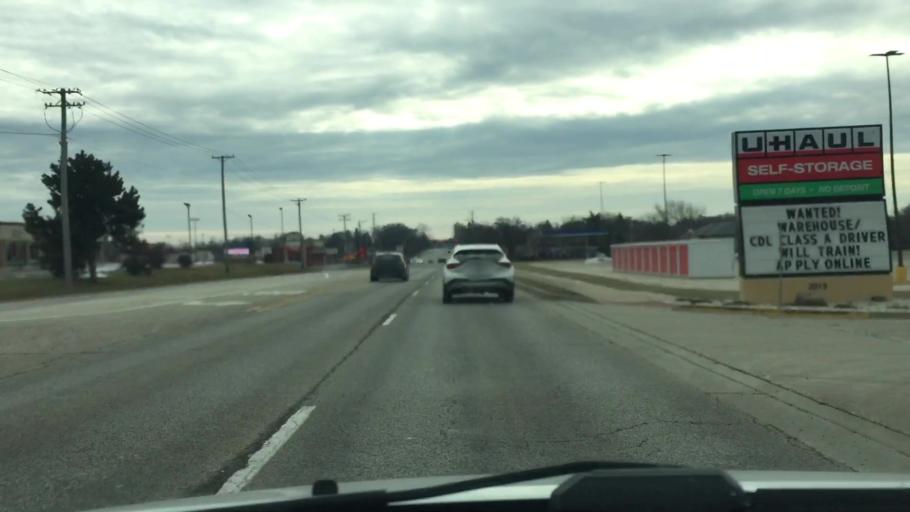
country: US
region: Illinois
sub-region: McHenry County
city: McHenry
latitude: 42.3567
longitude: -88.2675
